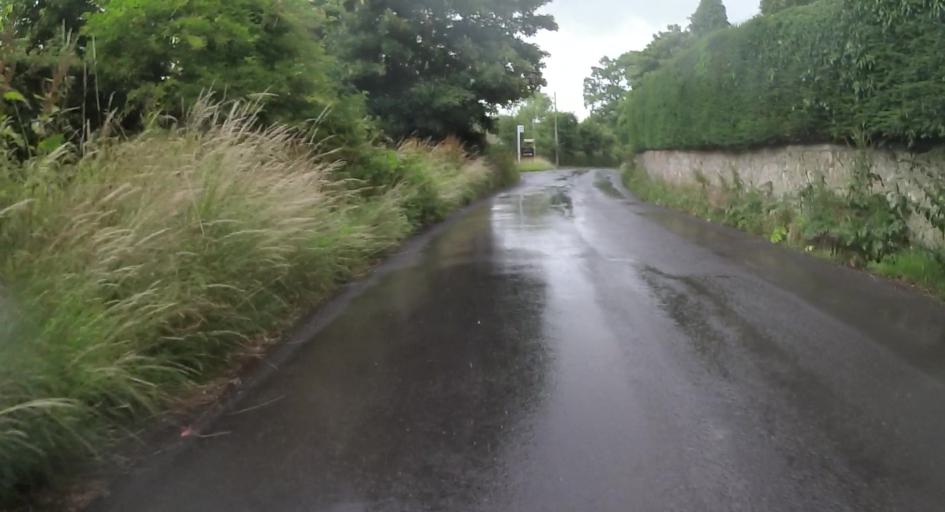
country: GB
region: England
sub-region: Hampshire
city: Long Sutton
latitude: 51.1800
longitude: -0.9216
